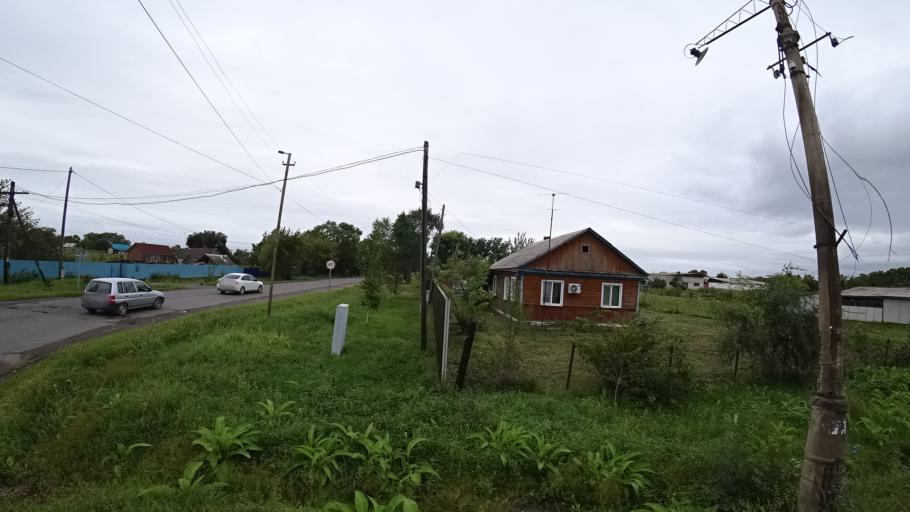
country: RU
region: Primorskiy
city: Chernigovka
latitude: 44.3449
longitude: 132.5683
